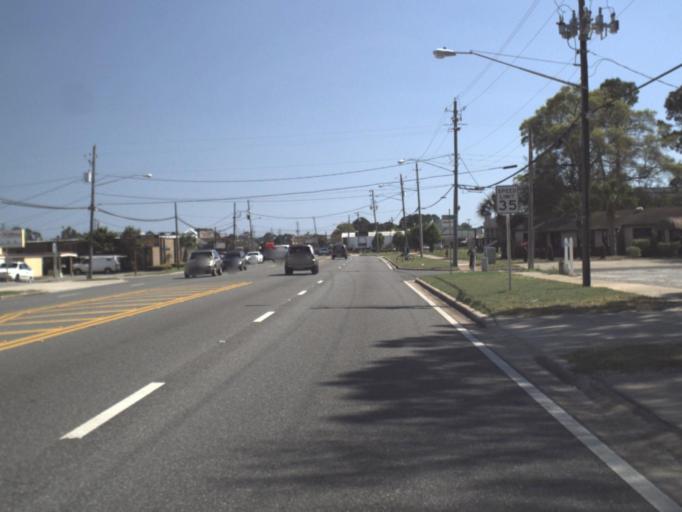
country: US
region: Florida
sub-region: Okaloosa County
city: Fort Walton Beach
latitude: 30.4181
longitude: -86.6138
